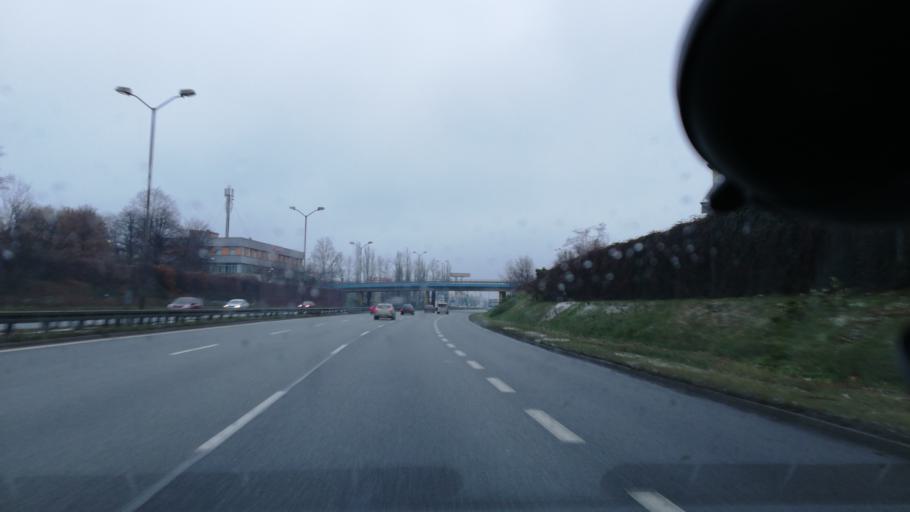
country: PL
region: Silesian Voivodeship
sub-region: Chorzow
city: Chorzow
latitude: 50.2817
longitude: 18.9503
